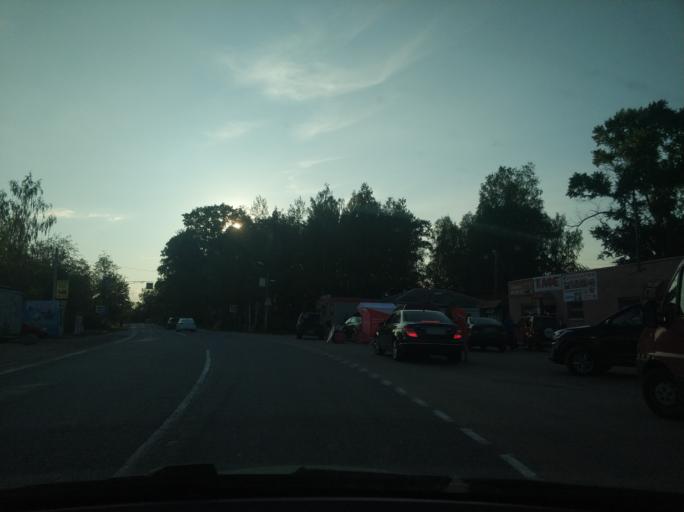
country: RU
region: Leningrad
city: Borisova Griva
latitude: 60.0943
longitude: 30.9753
